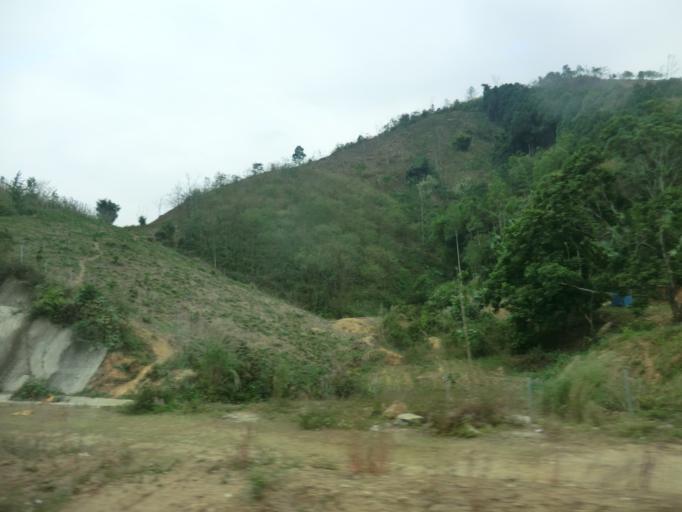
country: VN
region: Lao Cai
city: Thi Tran Pho Rang
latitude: 22.1068
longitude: 104.4101
